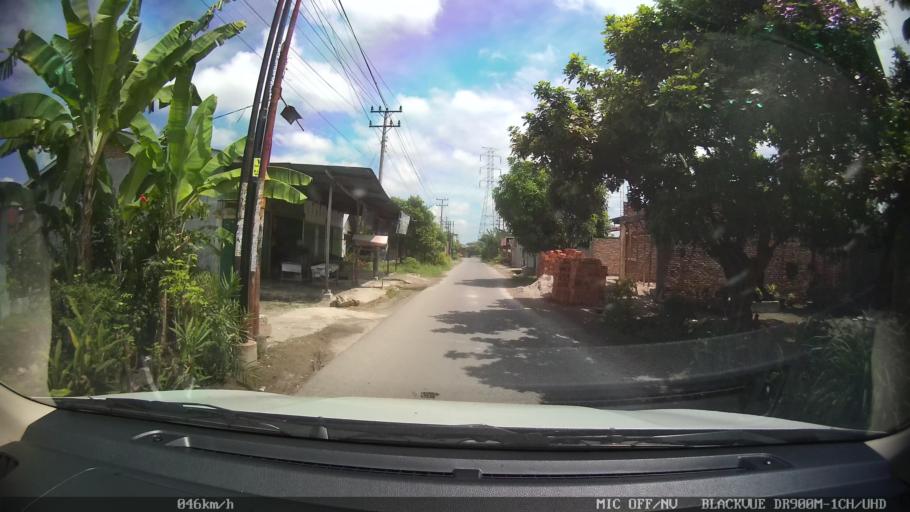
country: ID
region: North Sumatra
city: Percut
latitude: 3.6056
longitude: 98.7877
